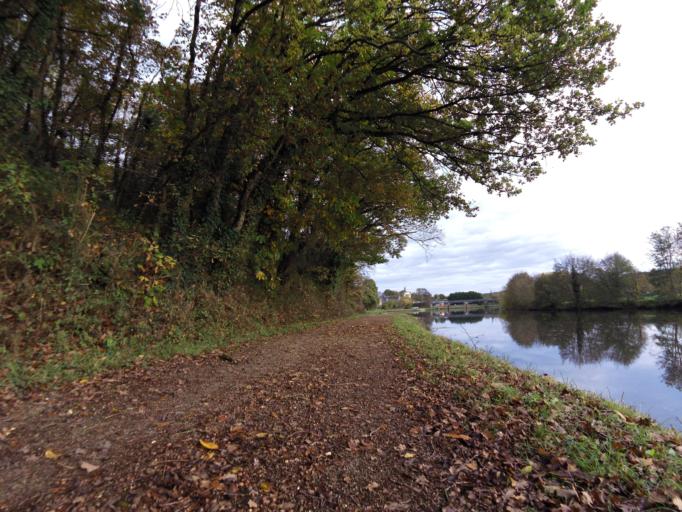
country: FR
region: Brittany
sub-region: Departement d'Ille-et-Vilaine
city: Bourg-des-Comptes
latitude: 47.9306
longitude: -1.7619
